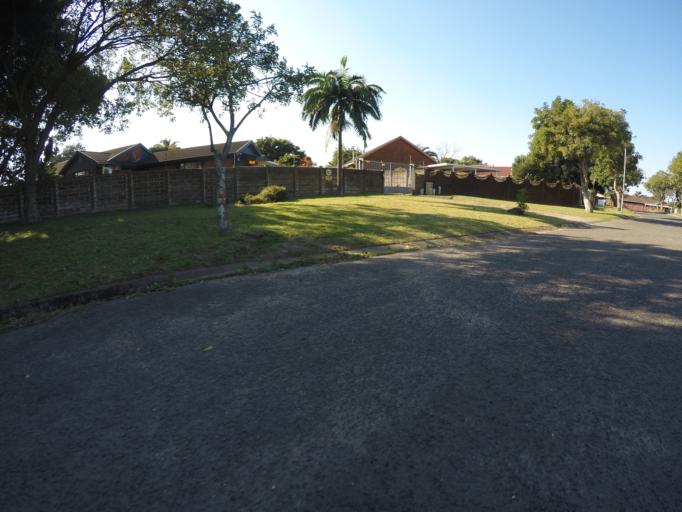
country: ZA
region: KwaZulu-Natal
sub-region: uThungulu District Municipality
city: Richards Bay
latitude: -28.7653
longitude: 32.0579
